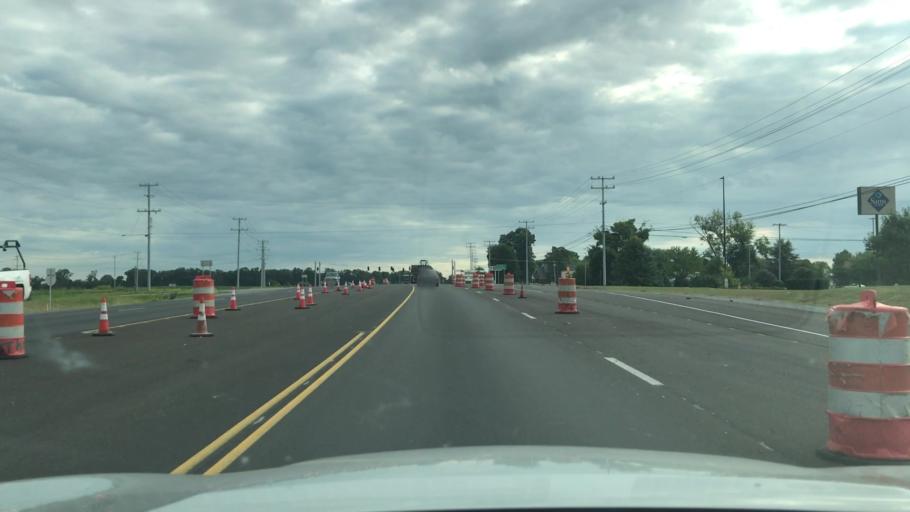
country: US
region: Tennessee
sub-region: Montgomery County
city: Clarksville
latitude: 36.6028
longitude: -87.2793
